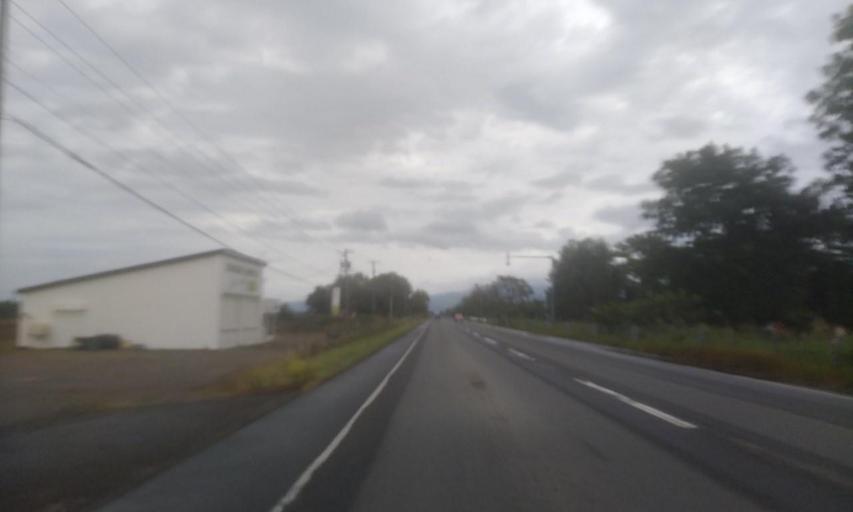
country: JP
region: Hokkaido
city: Abashiri
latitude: 43.8989
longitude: 144.6202
